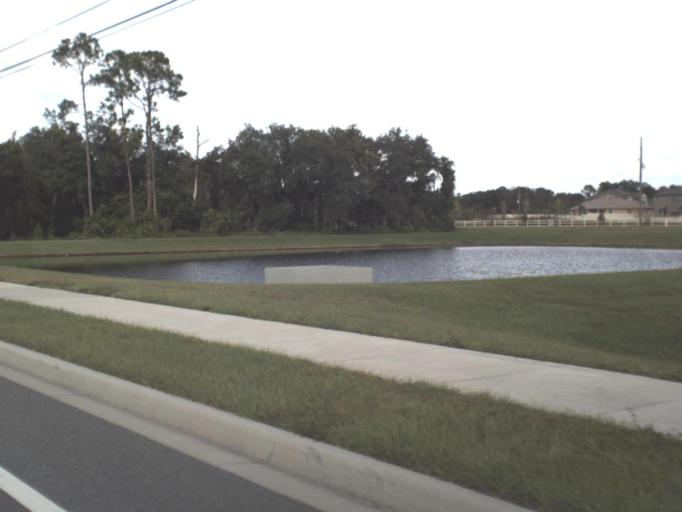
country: US
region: Florida
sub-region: Osceola County
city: Saint Cloud
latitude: 28.3026
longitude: -81.2391
